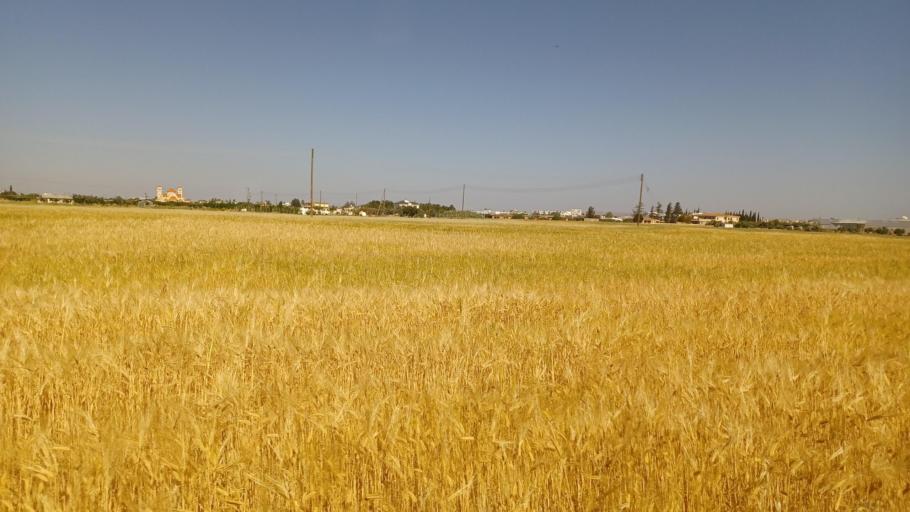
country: CY
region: Lefkosia
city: Kokkinotrimithia
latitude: 35.1455
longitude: 33.2193
